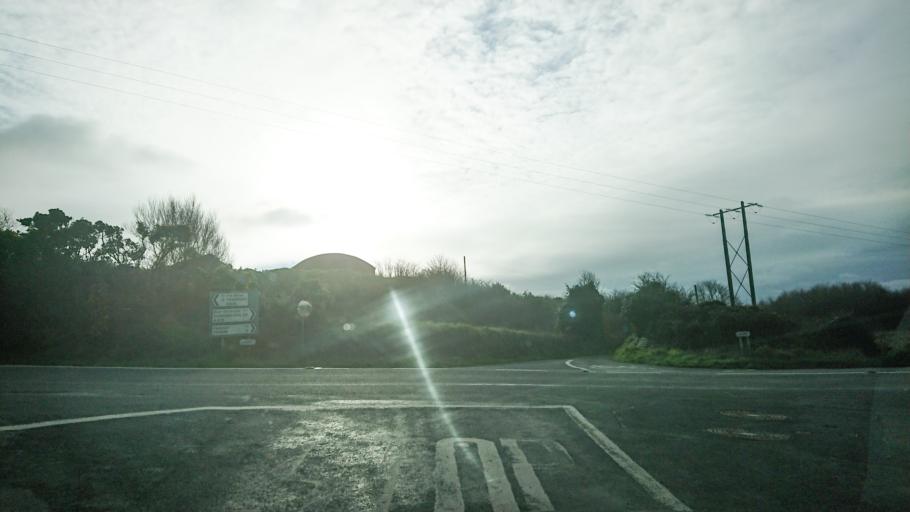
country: IE
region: Munster
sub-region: Waterford
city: Tra Mhor
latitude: 52.1559
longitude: -7.1902
